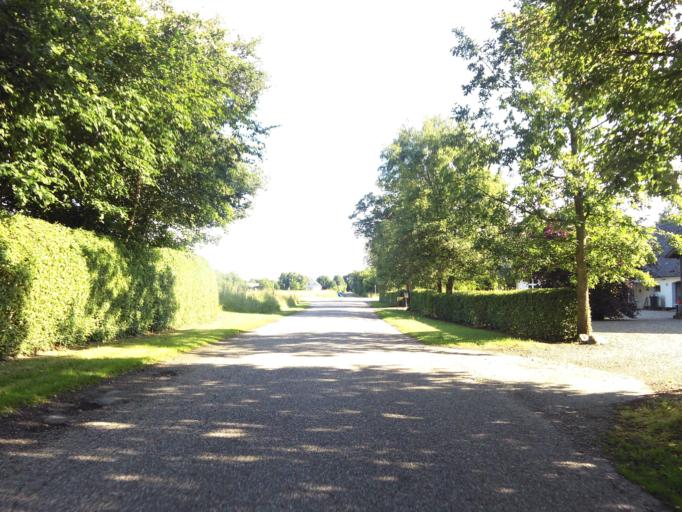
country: DK
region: South Denmark
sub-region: Vejen Kommune
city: Rodding
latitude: 55.3169
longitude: 9.1810
